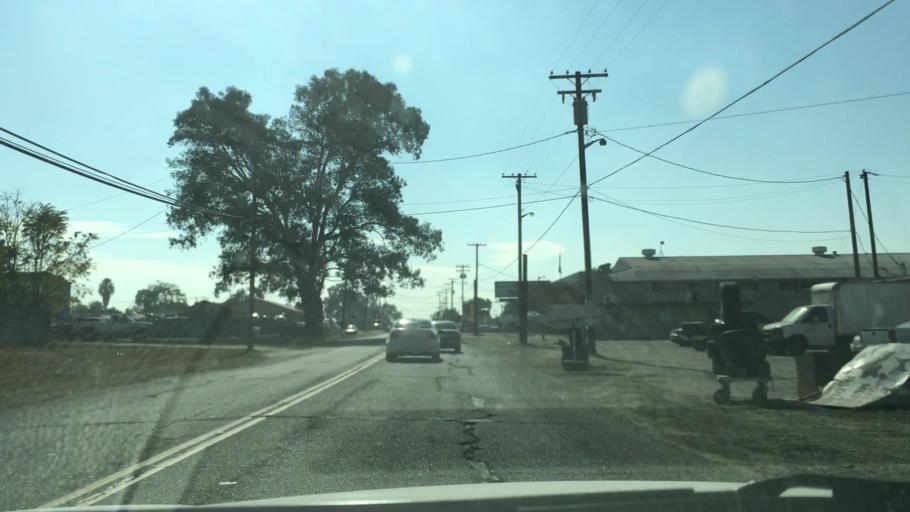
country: US
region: California
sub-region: Stanislaus County
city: Bystrom
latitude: 37.6232
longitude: -120.9936
